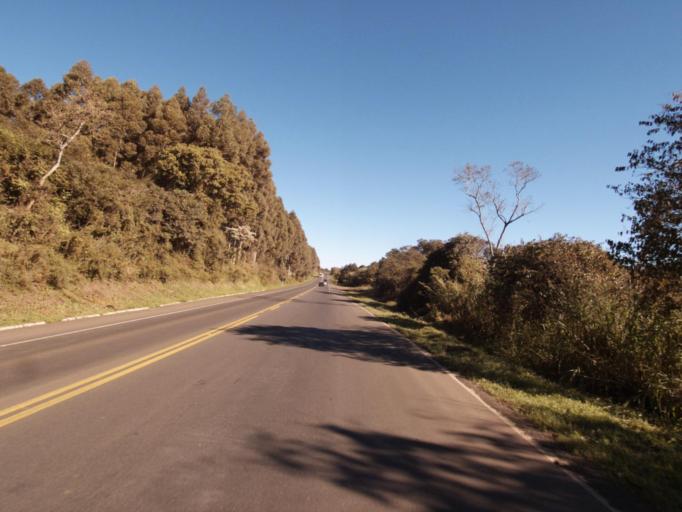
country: BR
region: Santa Catarina
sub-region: Xanxere
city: Xanxere
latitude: -26.9171
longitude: -52.4934
